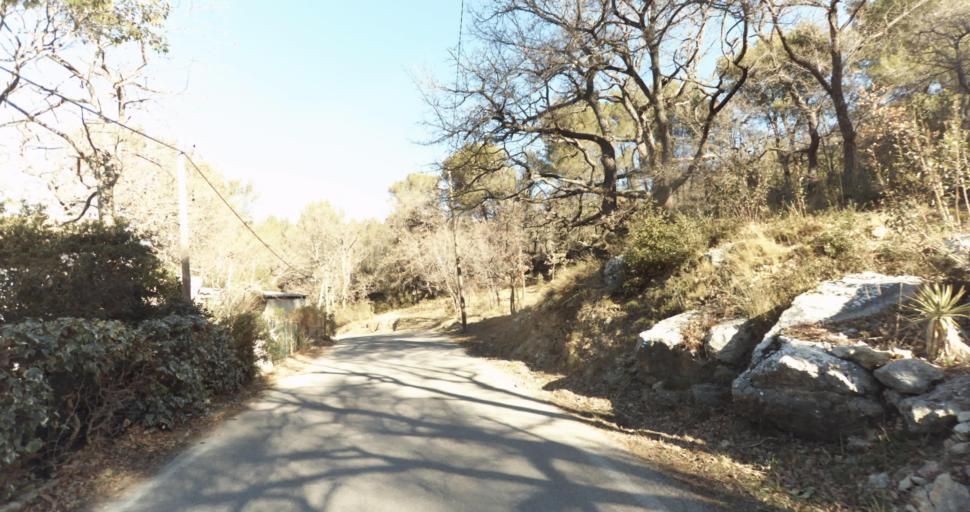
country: FR
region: Provence-Alpes-Cote d'Azur
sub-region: Departement des Bouches-du-Rhone
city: Peypin
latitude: 43.3647
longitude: 5.5675
